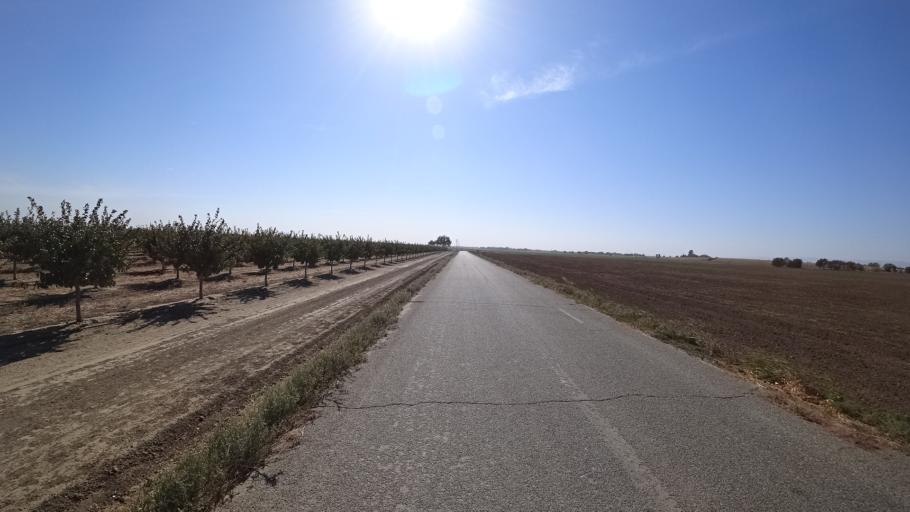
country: US
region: California
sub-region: Yolo County
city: Woodland
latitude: 38.6367
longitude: -121.7570
